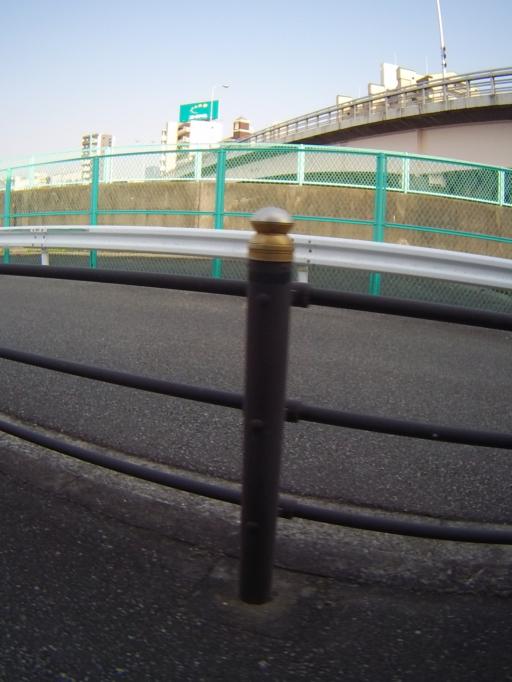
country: JP
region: Osaka
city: Osaka-shi
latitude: 34.6865
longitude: 135.4633
